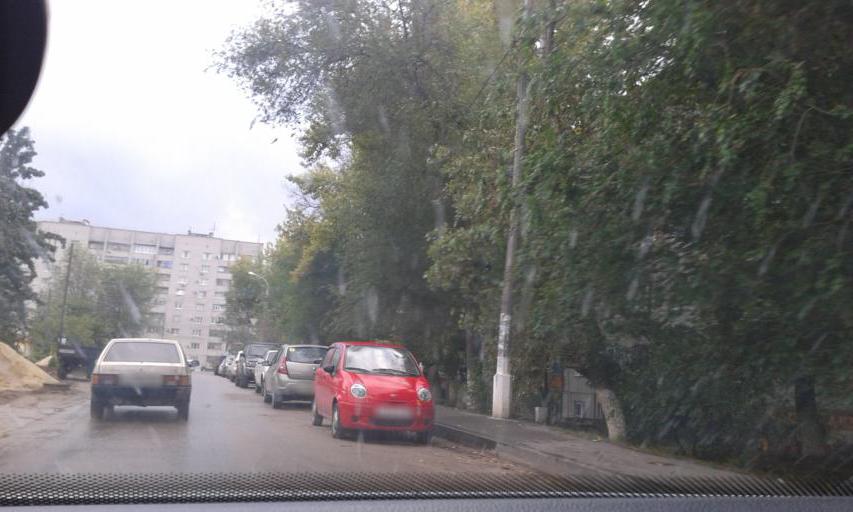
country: RU
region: Volgograd
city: Gorodishche
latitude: 48.7692
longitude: 44.4925
